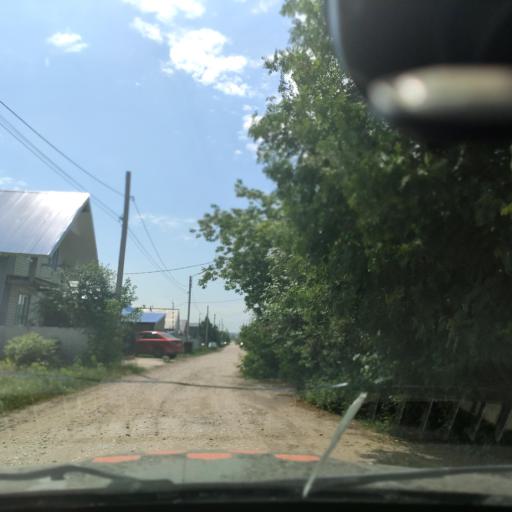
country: RU
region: Samara
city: Tol'yatti
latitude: 53.5756
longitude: 49.4084
